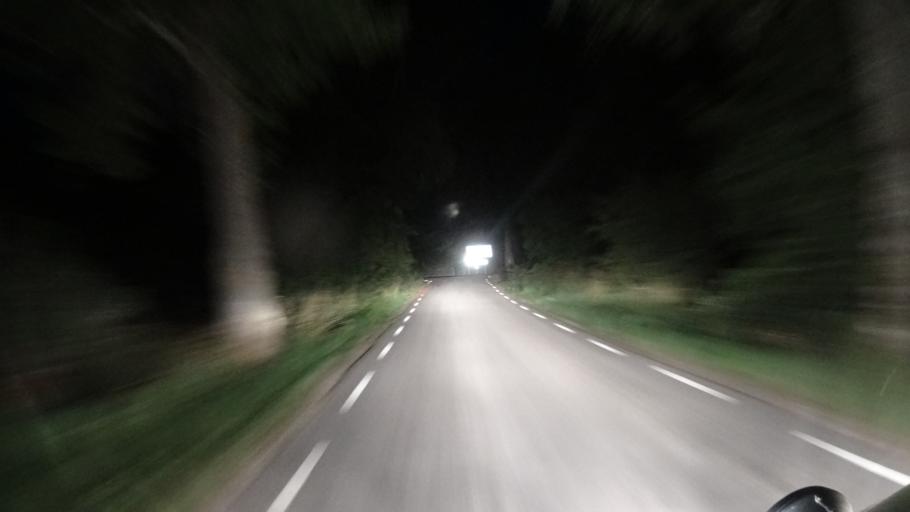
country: SE
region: OEstergoetland
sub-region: Vadstena Kommun
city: Herrestad
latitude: 58.3210
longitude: 14.8417
